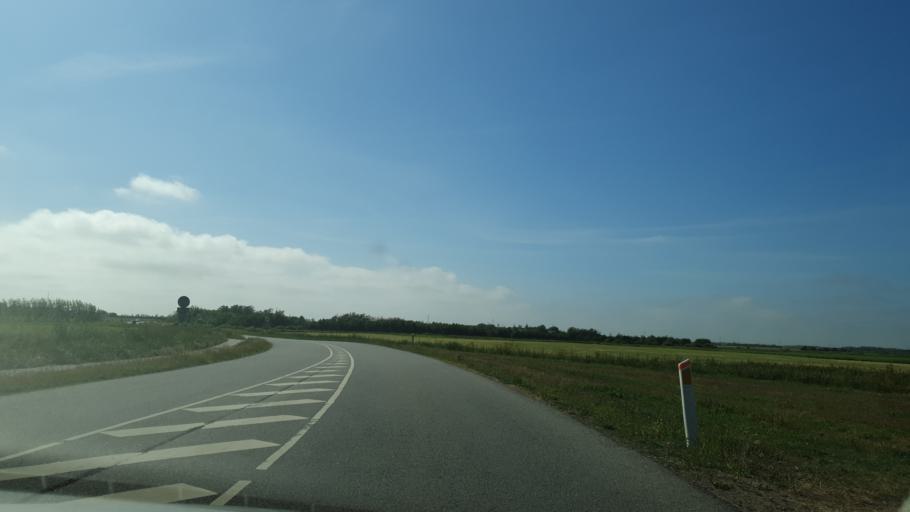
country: DK
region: Central Jutland
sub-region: Ringkobing-Skjern Kommune
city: Ringkobing
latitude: 56.0261
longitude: 8.3656
